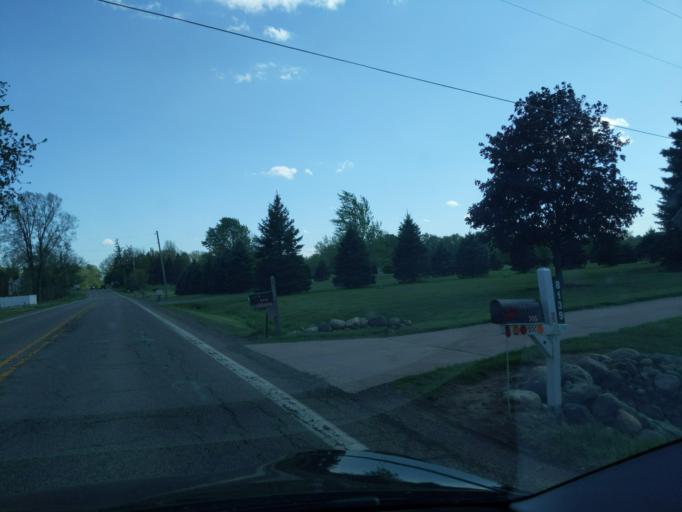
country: US
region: Michigan
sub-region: Eaton County
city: Potterville
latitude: 42.6850
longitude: -84.7396
